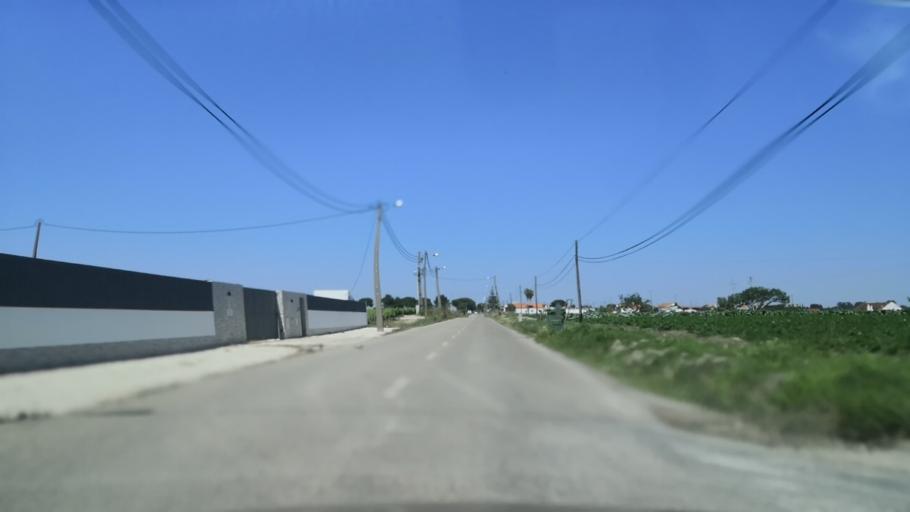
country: PT
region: Santarem
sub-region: Benavente
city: Poceirao
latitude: 38.6712
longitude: -8.7356
